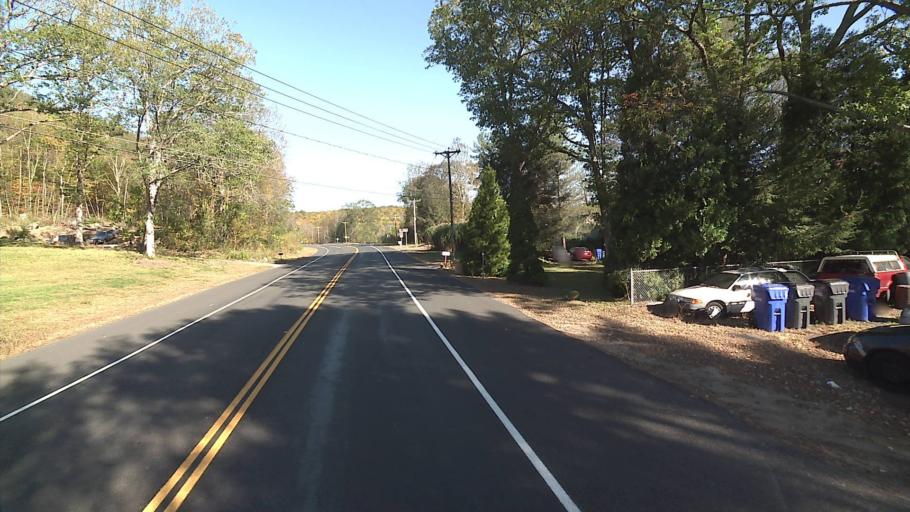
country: US
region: Connecticut
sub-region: Tolland County
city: Coventry Lake
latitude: 41.7663
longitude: -72.4061
